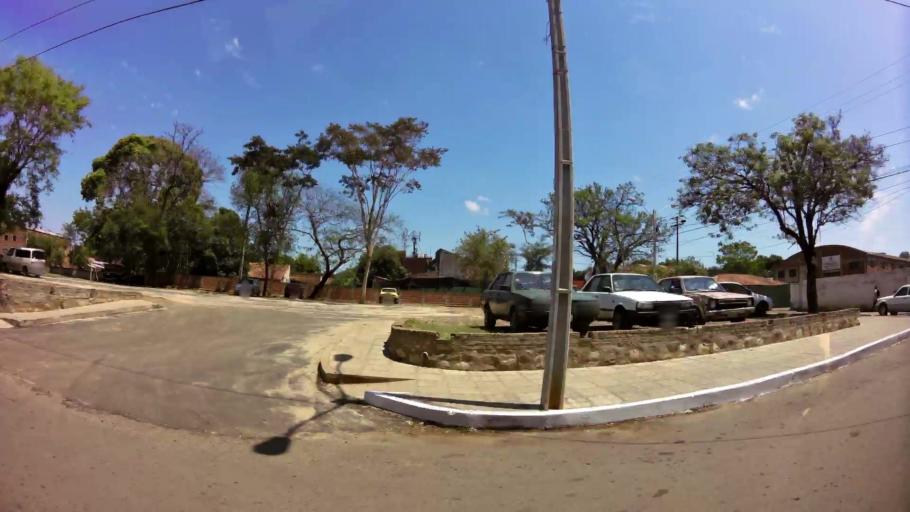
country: PY
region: Central
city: Fernando de la Mora
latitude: -25.3252
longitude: -57.5531
